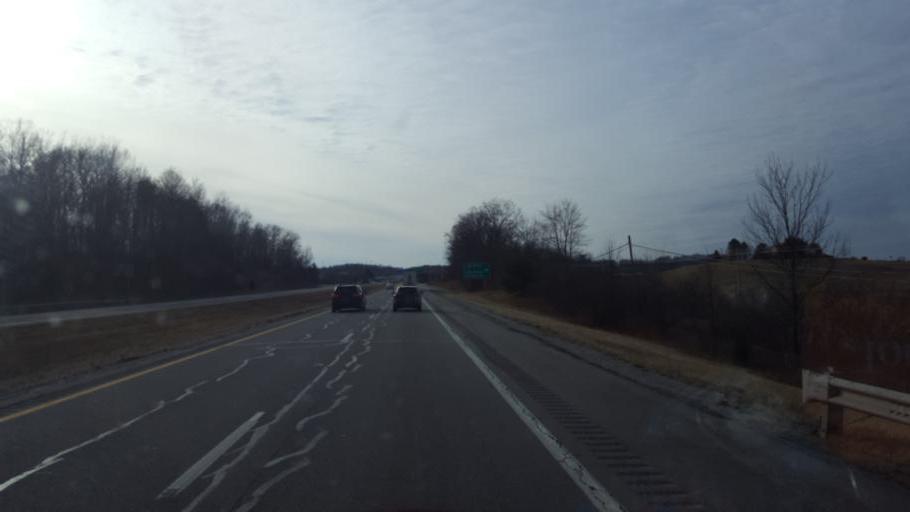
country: US
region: Ohio
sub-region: Richland County
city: Lincoln Heights
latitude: 40.7864
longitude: -82.3995
